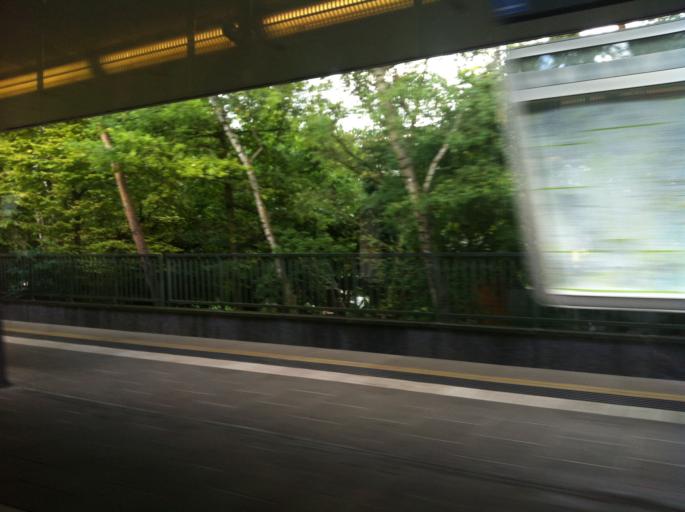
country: DE
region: Bavaria
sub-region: Upper Bavaria
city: Unterfoehring
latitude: 48.2034
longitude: 11.6132
